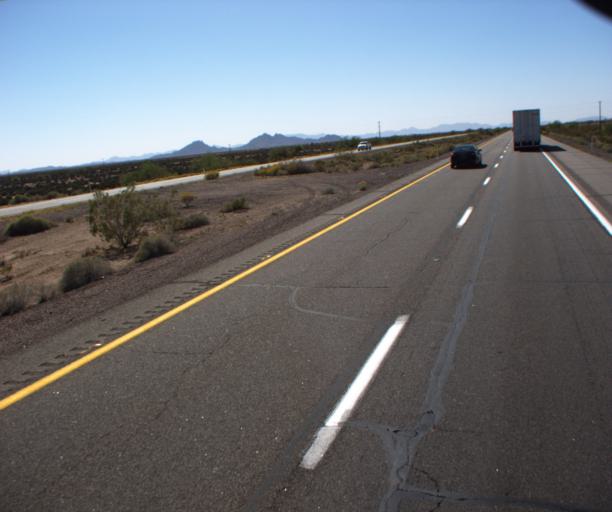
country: US
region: Arizona
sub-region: Yuma County
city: Wellton
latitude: 32.7034
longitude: -113.8894
